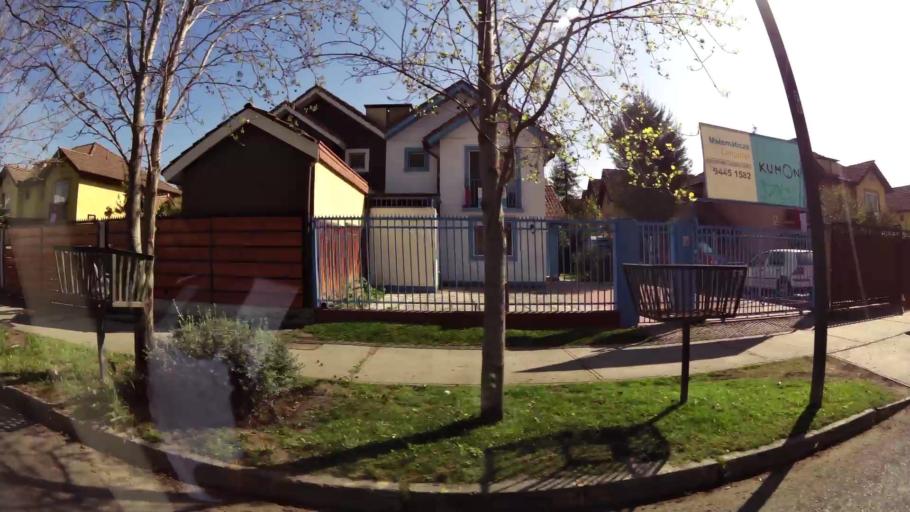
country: CL
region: Santiago Metropolitan
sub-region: Provincia de Chacabuco
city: Chicureo Abajo
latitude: -33.3529
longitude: -70.6736
